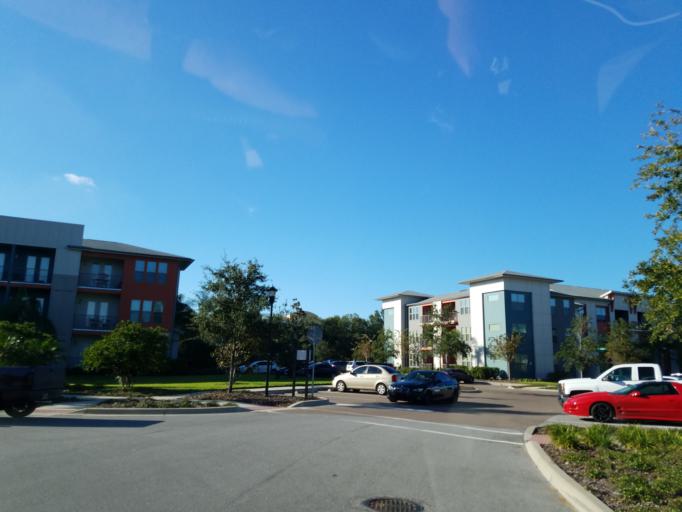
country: US
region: Florida
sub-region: Hillsborough County
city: Palm River-Clair Mel
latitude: 27.9388
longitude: -82.3364
